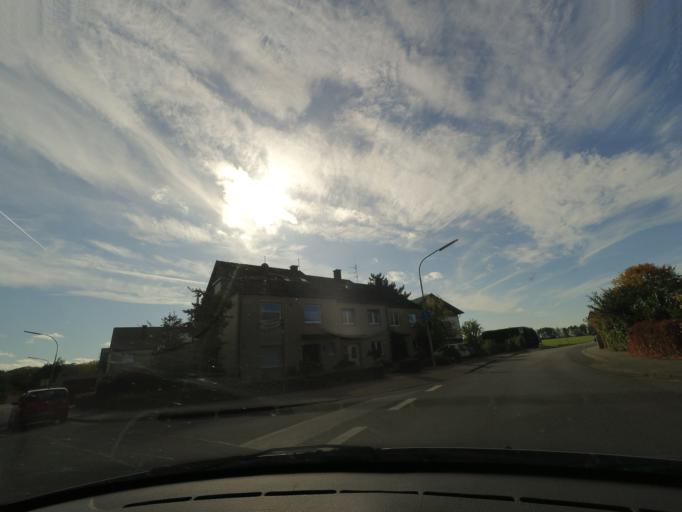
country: DE
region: North Rhine-Westphalia
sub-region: Regierungsbezirk Dusseldorf
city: Korschenbroich
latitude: 51.1626
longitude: 6.5724
